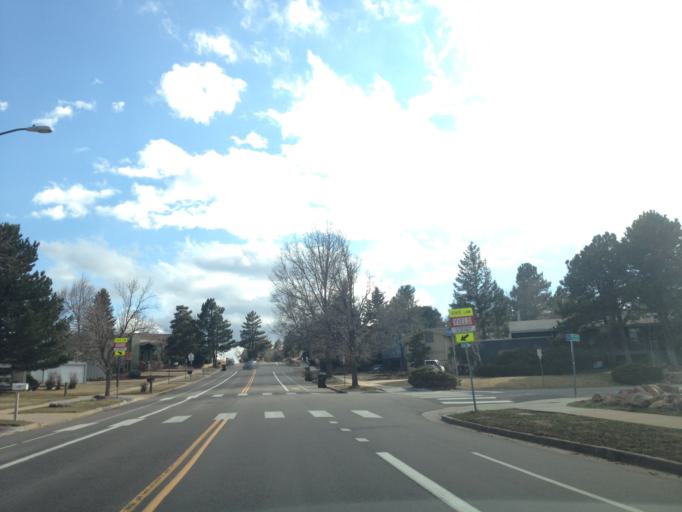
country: US
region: Colorado
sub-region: Boulder County
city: Boulder
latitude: 39.9707
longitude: -105.2468
